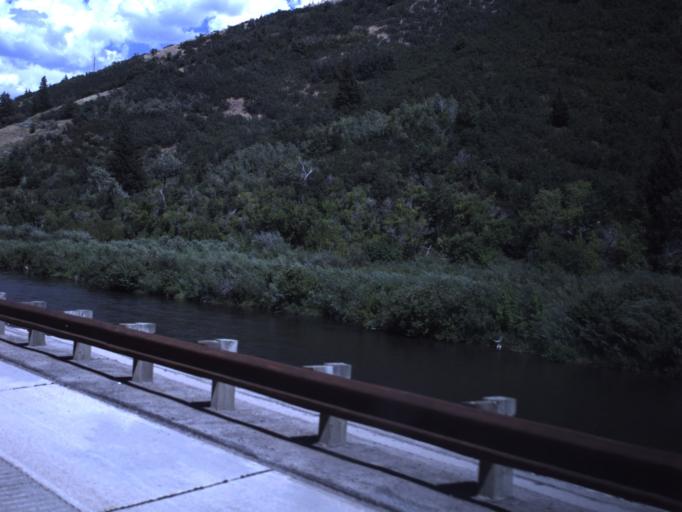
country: US
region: Utah
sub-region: Utah County
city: Orem
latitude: 40.3690
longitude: -111.5551
